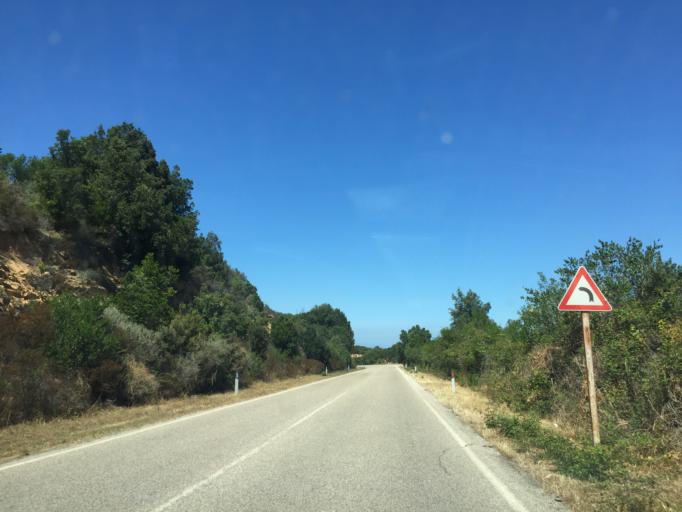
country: IT
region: Sardinia
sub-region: Provincia di Olbia-Tempio
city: Aglientu
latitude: 41.0868
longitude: 9.1180
